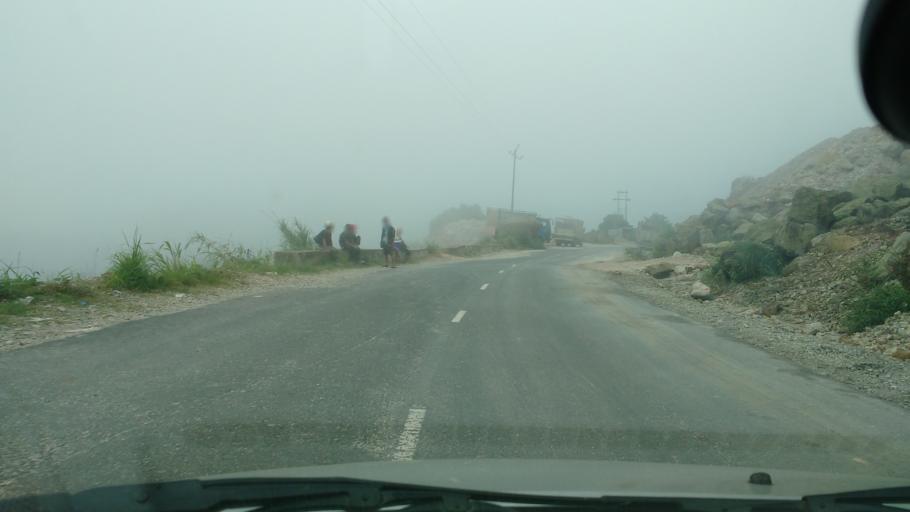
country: IN
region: Meghalaya
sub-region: East Khasi Hills
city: Cherrapunji
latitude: 25.3702
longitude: 91.8759
